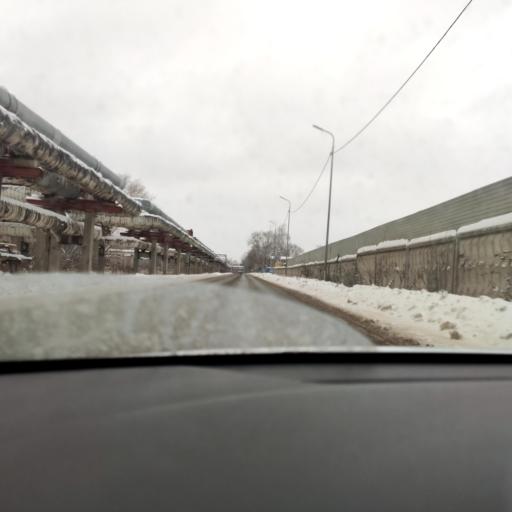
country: RU
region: Tatarstan
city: Staroye Arakchino
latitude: 55.8655
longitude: 48.9482
